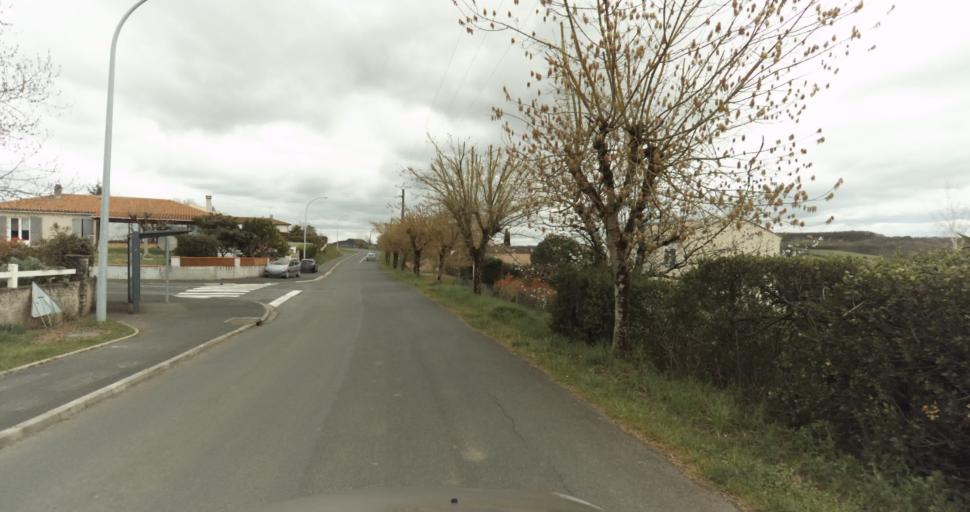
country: FR
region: Midi-Pyrenees
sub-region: Departement du Tarn
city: Puygouzon
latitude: 43.8919
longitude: 2.1784
